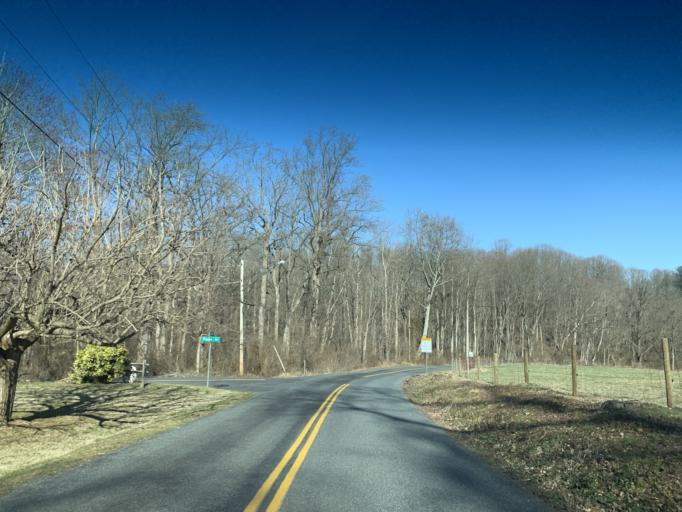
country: US
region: Maryland
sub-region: Harford County
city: Aberdeen
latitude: 39.6306
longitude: -76.2287
